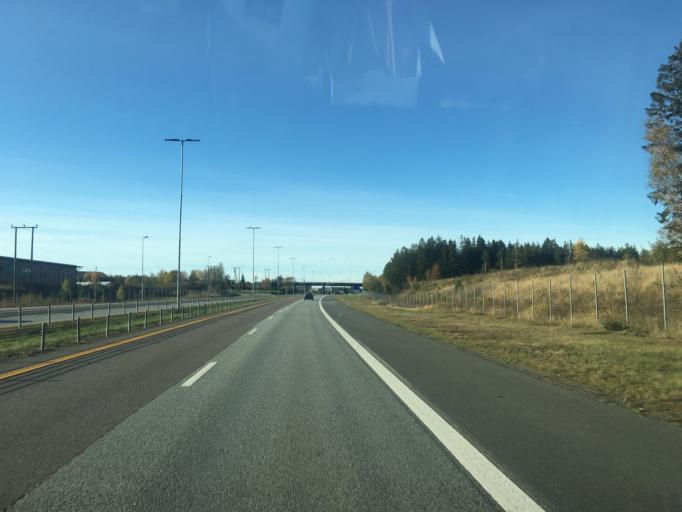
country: NO
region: Ostfold
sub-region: Rade
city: Karlshus
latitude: 59.3570
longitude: 10.8499
